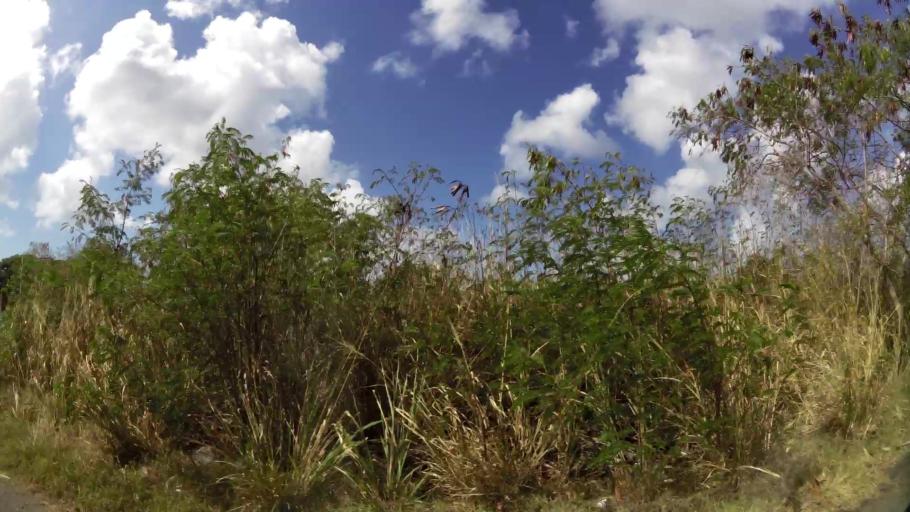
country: KN
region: Saint Thomas Lowland
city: Cotton Ground
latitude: 17.1846
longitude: -62.6188
